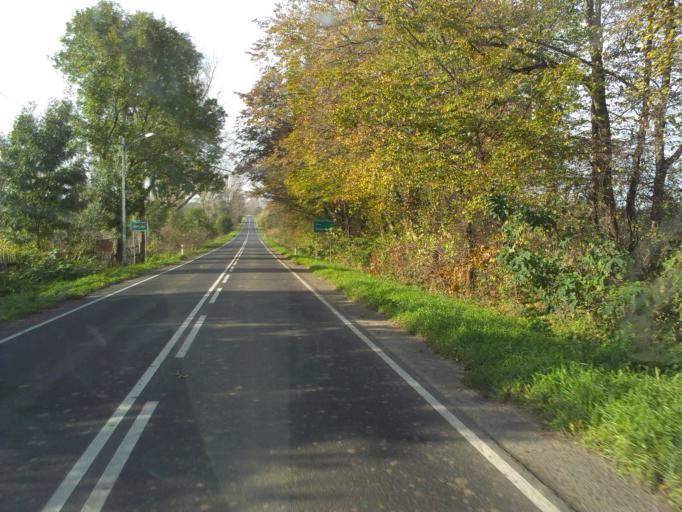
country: PL
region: West Pomeranian Voivodeship
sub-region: Powiat pyrzycki
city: Kozielice
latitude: 53.1301
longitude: 14.8280
